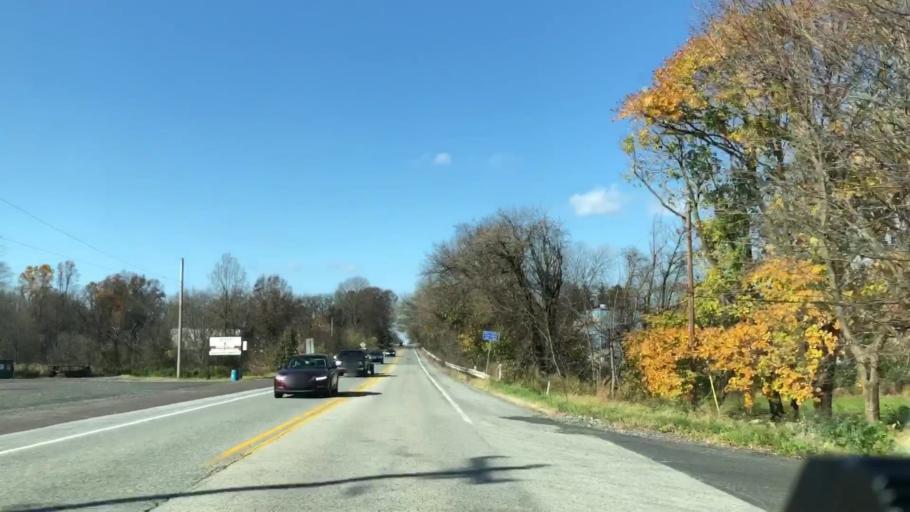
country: US
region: Pennsylvania
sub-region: Montgomery County
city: Sanatoga
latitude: 40.2076
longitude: -75.5931
